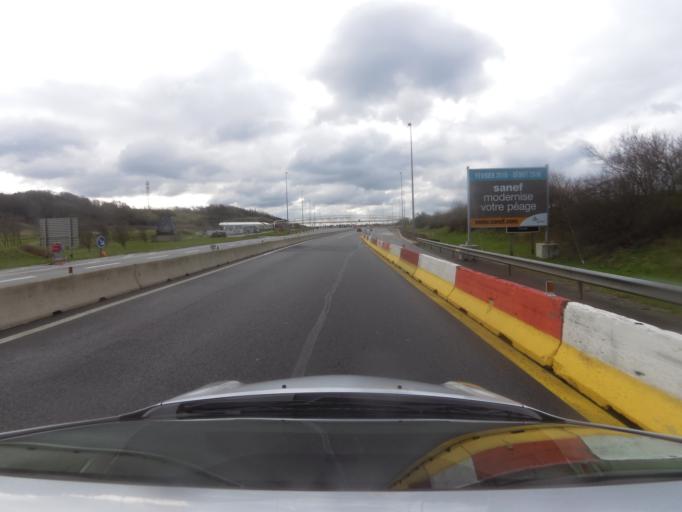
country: FR
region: Nord-Pas-de-Calais
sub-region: Departement du Pas-de-Calais
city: Saint-Leonard
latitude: 50.6917
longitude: 1.6397
